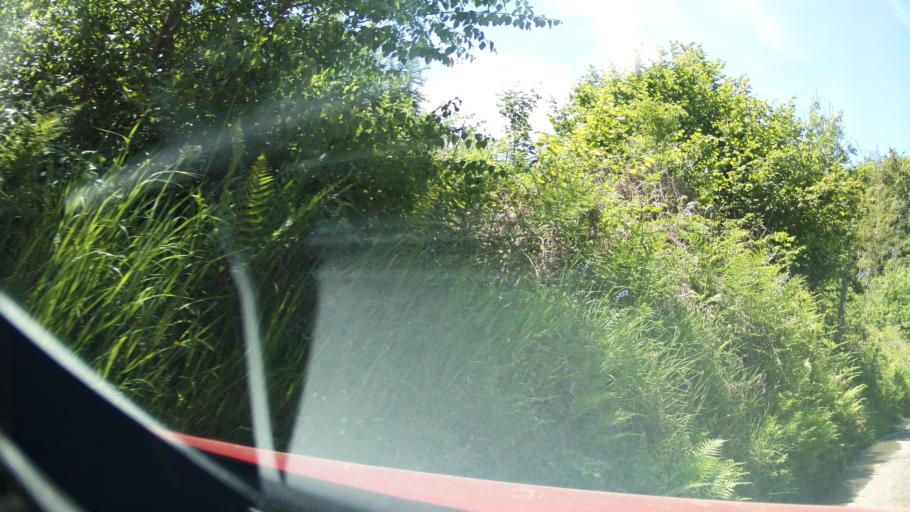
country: GB
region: Wales
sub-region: Monmouthshire
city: Llangwm
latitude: 51.6699
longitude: -2.7645
